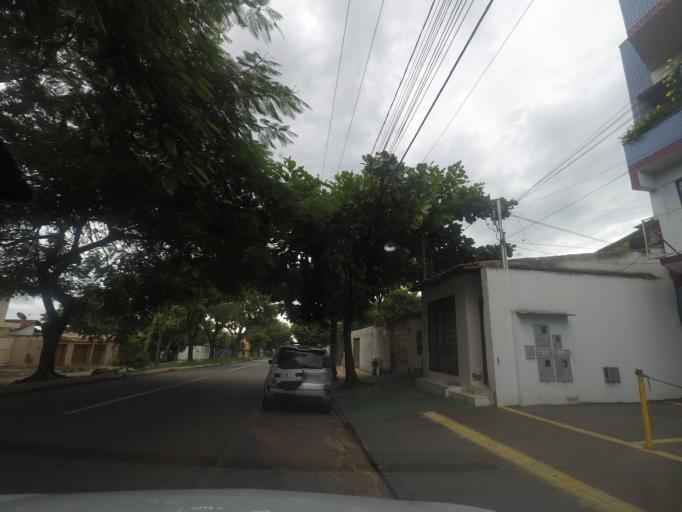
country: BR
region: Goias
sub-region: Goiania
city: Goiania
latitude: -16.6854
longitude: -49.2391
